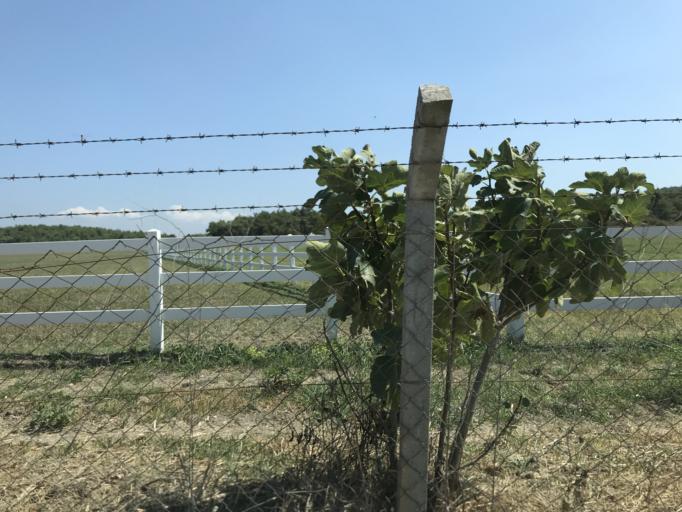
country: TR
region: Izmir
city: Urla
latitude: 38.2878
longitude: 26.7196
